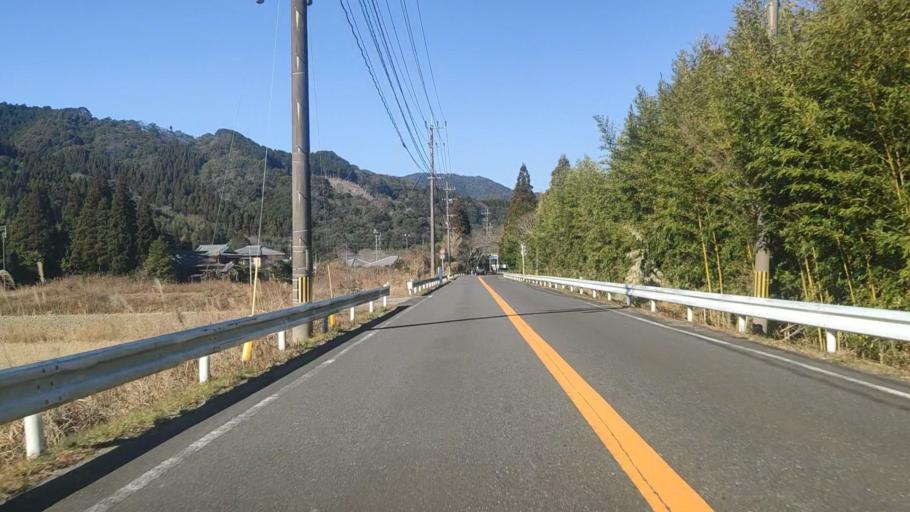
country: JP
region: Oita
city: Saiki
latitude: 32.9002
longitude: 131.9351
